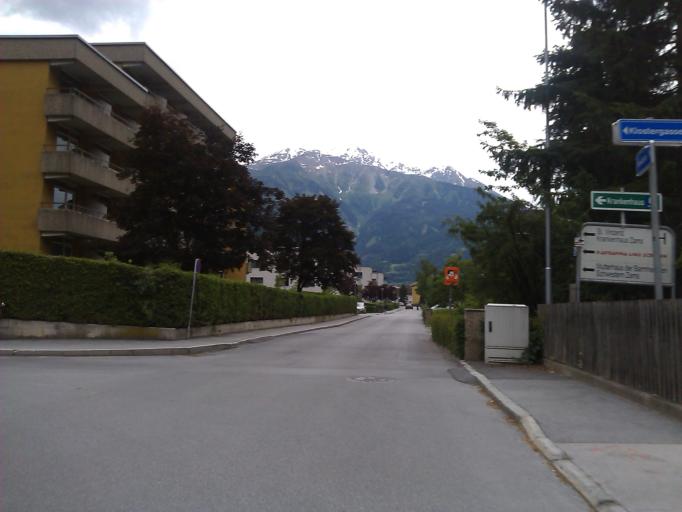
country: AT
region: Tyrol
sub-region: Politischer Bezirk Landeck
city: Zams
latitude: 47.1626
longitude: 10.5902
